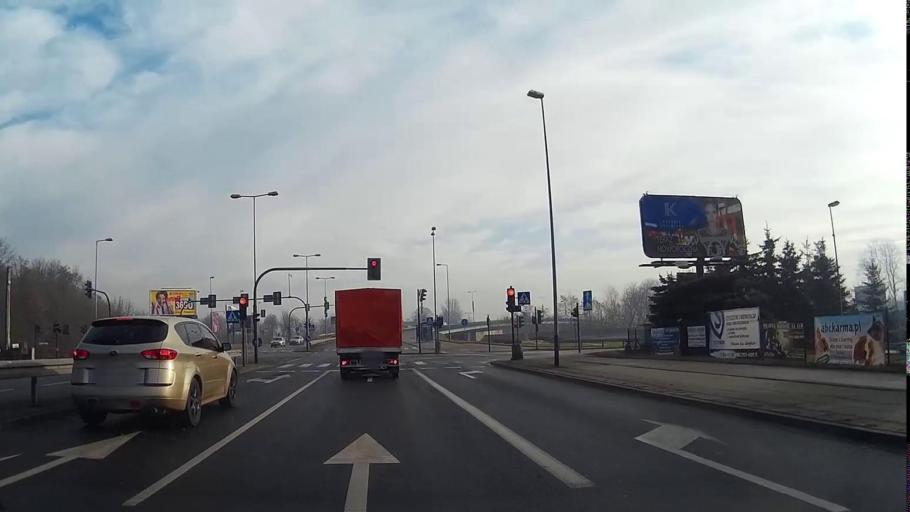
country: PL
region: Lesser Poland Voivodeship
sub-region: Krakow
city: Krakow
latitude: 50.0489
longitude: 19.9030
